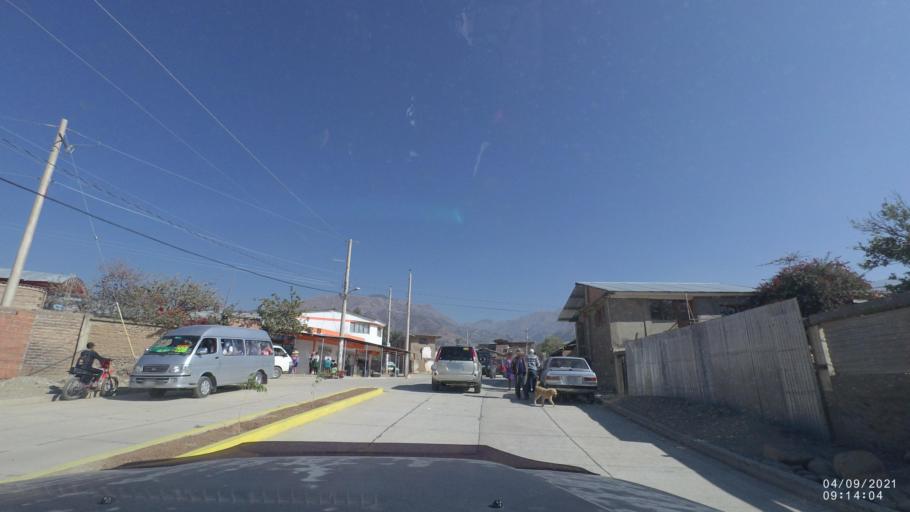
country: BO
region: Cochabamba
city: Sipe Sipe
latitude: -17.3814
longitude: -66.3457
